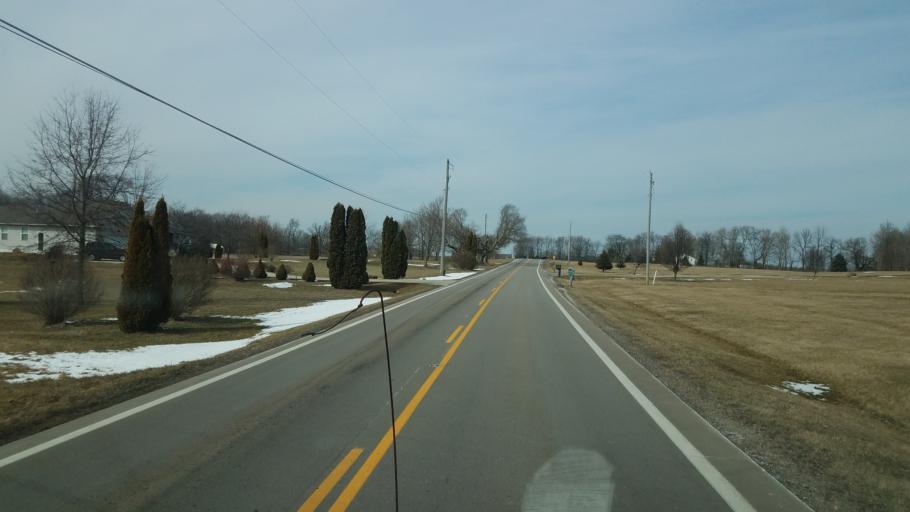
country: US
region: Ohio
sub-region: Delaware County
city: Delaware
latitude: 40.3566
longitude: -83.1427
